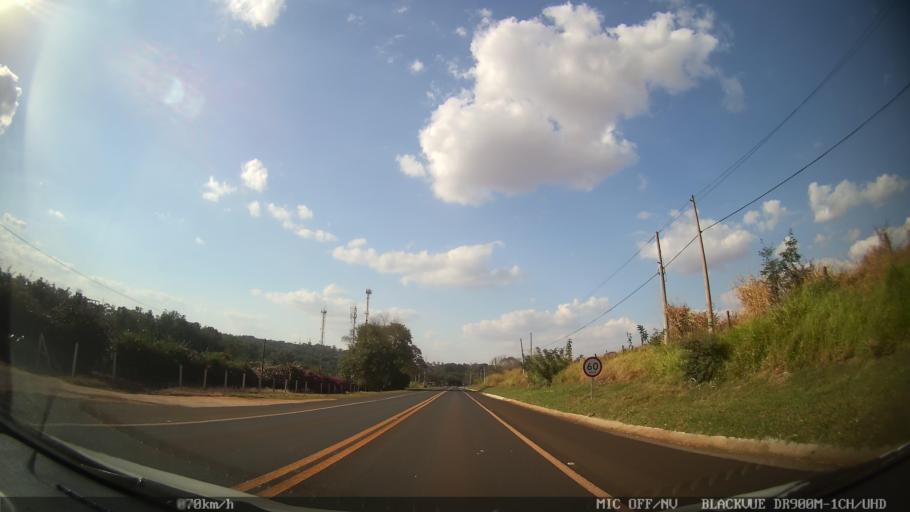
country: BR
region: Sao Paulo
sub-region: Ribeirao Preto
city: Ribeirao Preto
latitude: -21.1790
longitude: -47.8554
